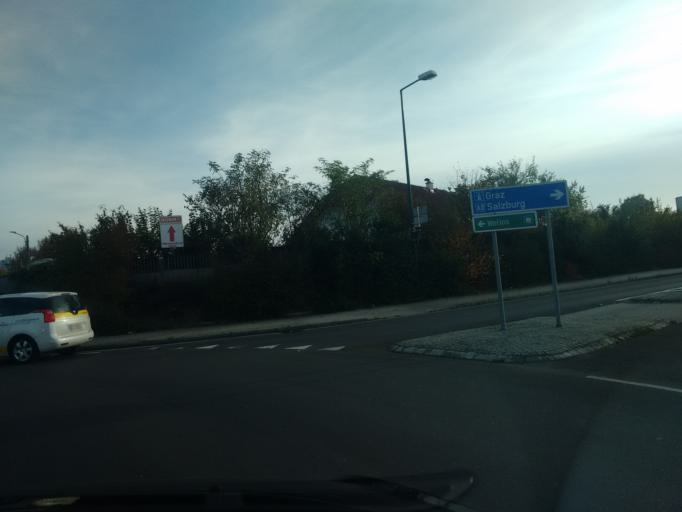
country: AT
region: Upper Austria
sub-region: Wels-Land
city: Gunskirchen
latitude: 48.1508
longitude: 13.9869
